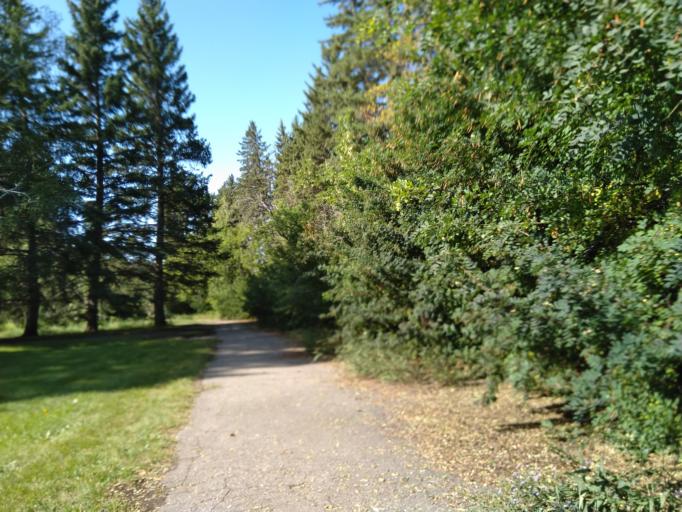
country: CA
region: Alberta
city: Calgary
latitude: 51.1008
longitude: -114.2247
